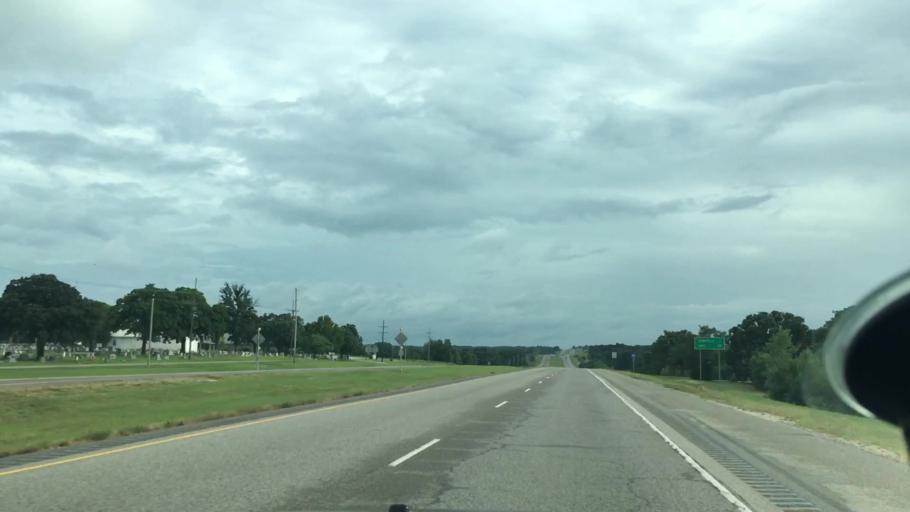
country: US
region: Oklahoma
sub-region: Seminole County
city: Seminole
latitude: 35.3474
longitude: -96.6719
